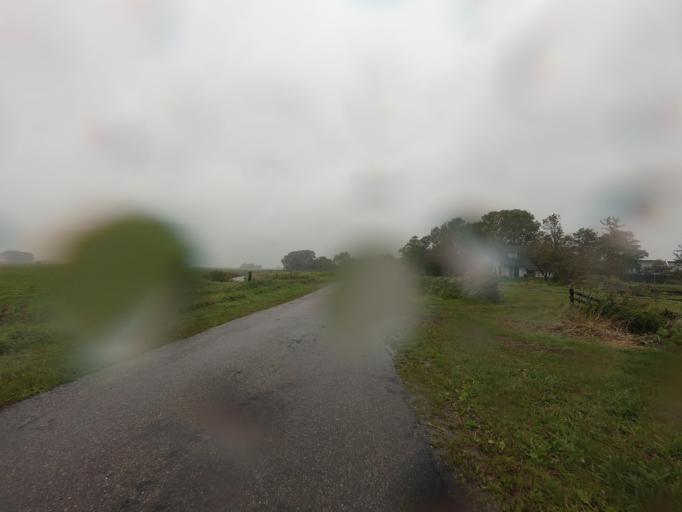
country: NL
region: Friesland
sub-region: Gemeente Boarnsterhim
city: Aldeboarn
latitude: 53.0603
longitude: 5.9176
